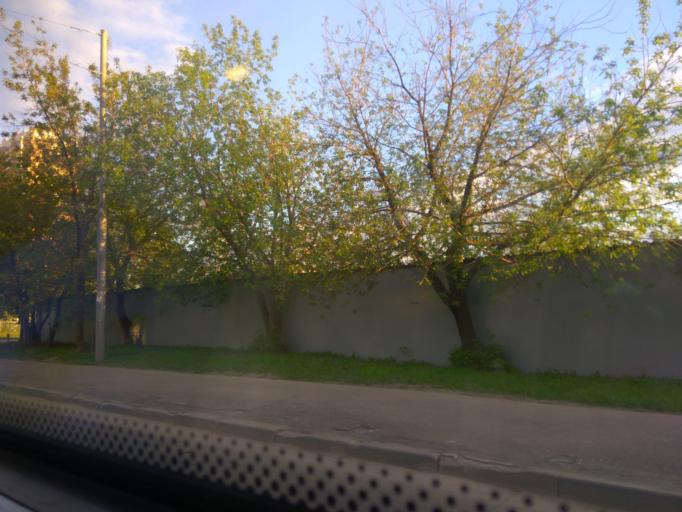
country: RU
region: Moscow
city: Tsaritsyno
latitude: 55.6479
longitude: 37.6481
